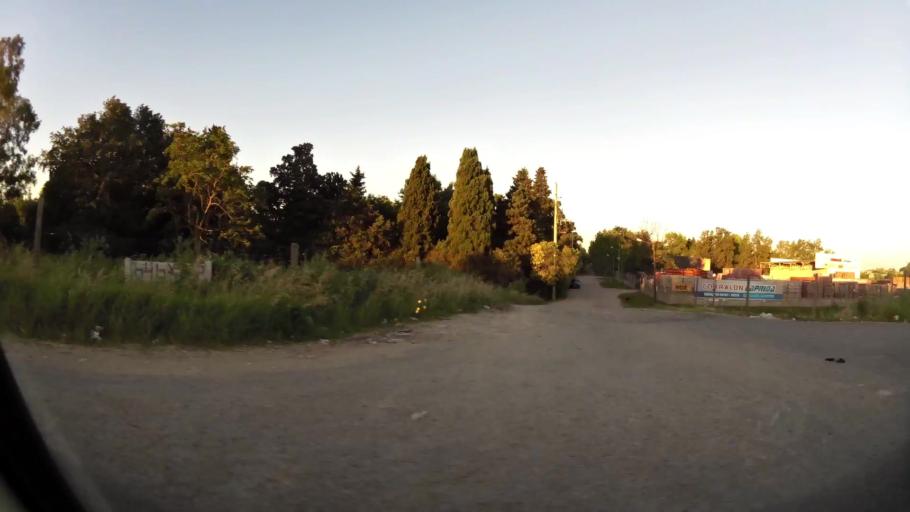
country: AR
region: Buenos Aires
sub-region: Partido de Quilmes
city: Quilmes
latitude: -34.8211
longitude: -58.1913
